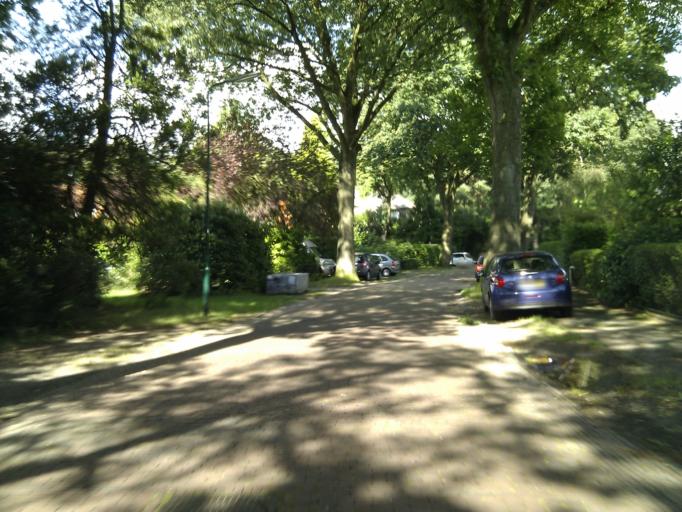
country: NL
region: Utrecht
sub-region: Gemeente De Bilt
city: De Bilt
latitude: 52.1368
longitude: 5.2184
